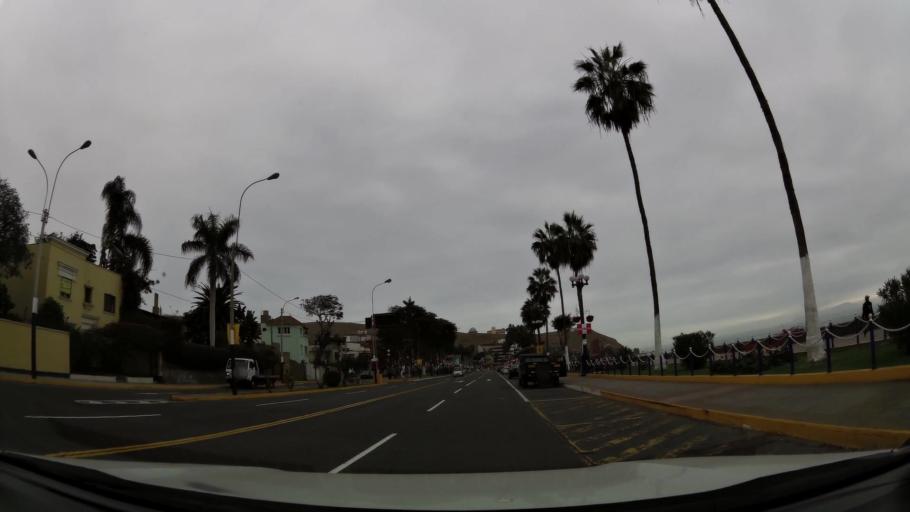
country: PE
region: Lima
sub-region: Lima
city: Surco
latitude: -12.1664
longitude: -77.0271
